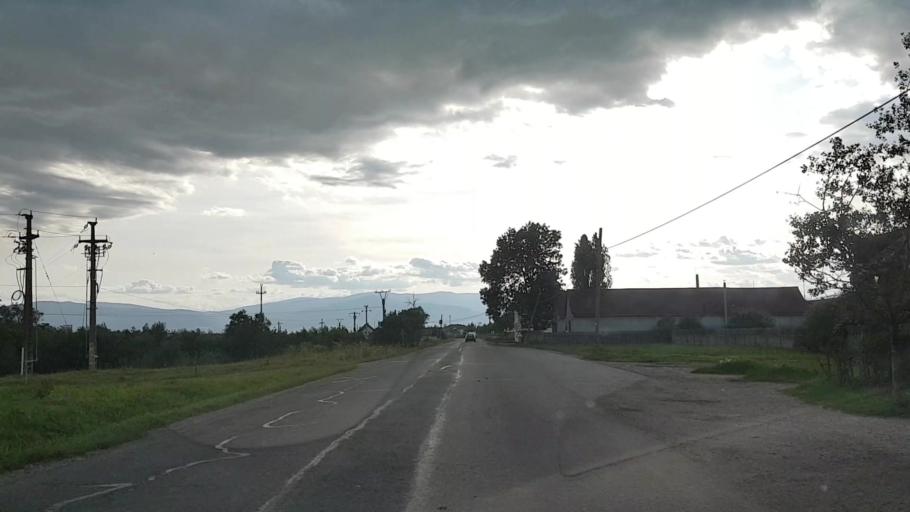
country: RO
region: Harghita
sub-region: Comuna Ciumani
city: Ciumani
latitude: 46.7076
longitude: 25.5347
